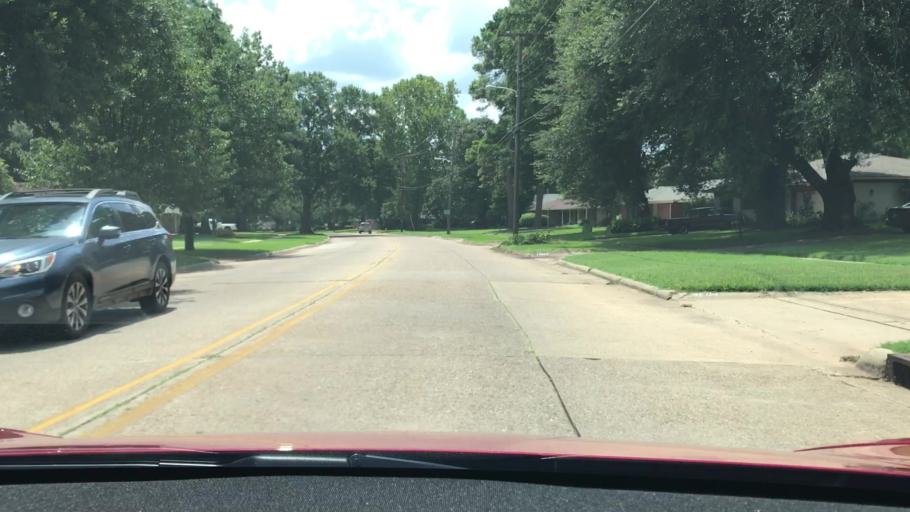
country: US
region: Louisiana
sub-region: Bossier Parish
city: Bossier City
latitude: 32.4592
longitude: -93.7340
